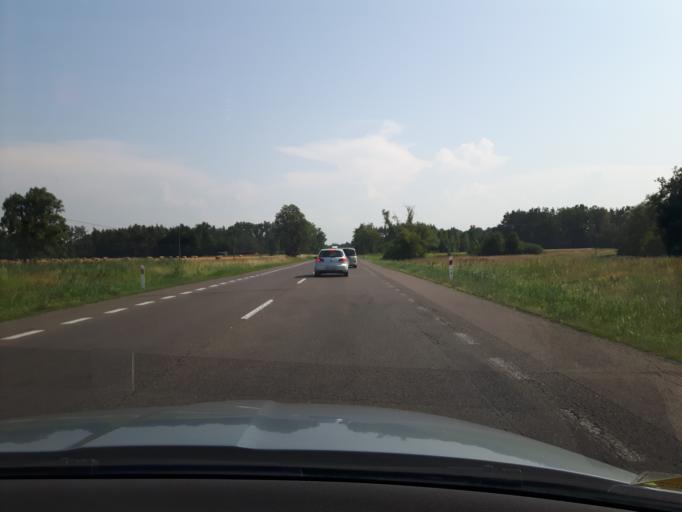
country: PL
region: Masovian Voivodeship
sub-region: Powiat plonski
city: Baboszewo
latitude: 52.7161
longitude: 20.3273
